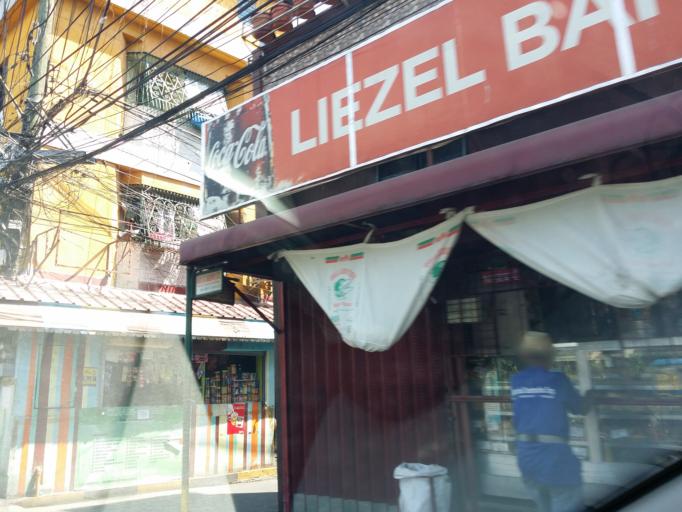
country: PH
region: Metro Manila
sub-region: Mandaluyong
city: Mandaluyong City
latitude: 14.5789
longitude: 121.0264
